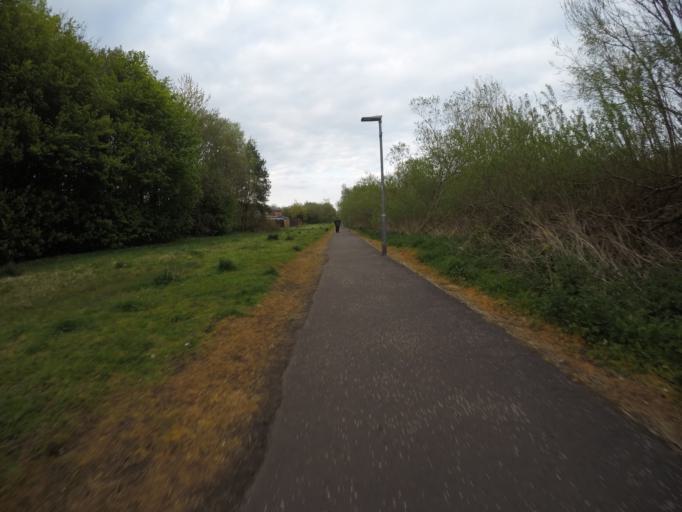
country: GB
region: Scotland
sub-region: North Ayrshire
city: Irvine
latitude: 55.6341
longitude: -4.6384
